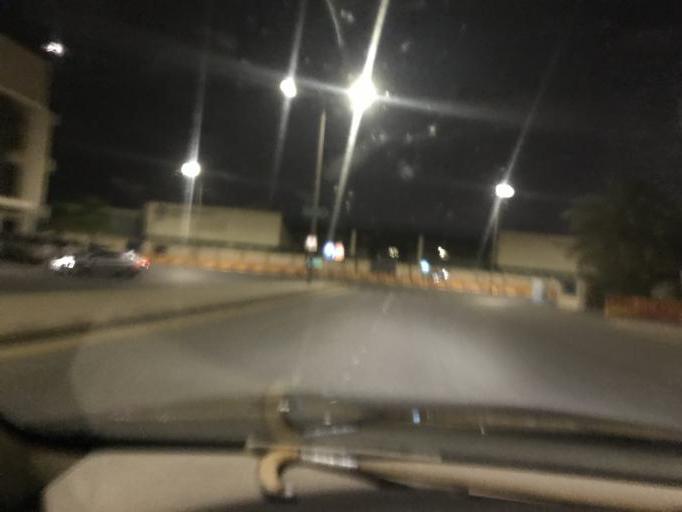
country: SA
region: Ar Riyad
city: Riyadh
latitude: 24.7975
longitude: 46.7085
